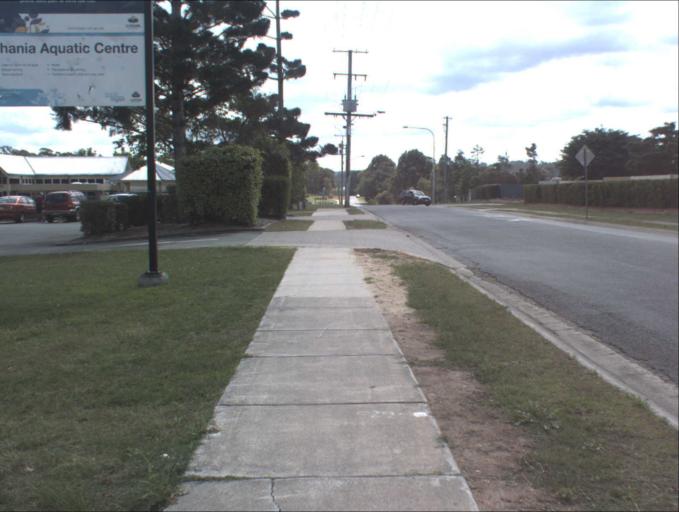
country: AU
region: Queensland
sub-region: Logan
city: Waterford West
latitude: -27.6868
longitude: 153.1575
